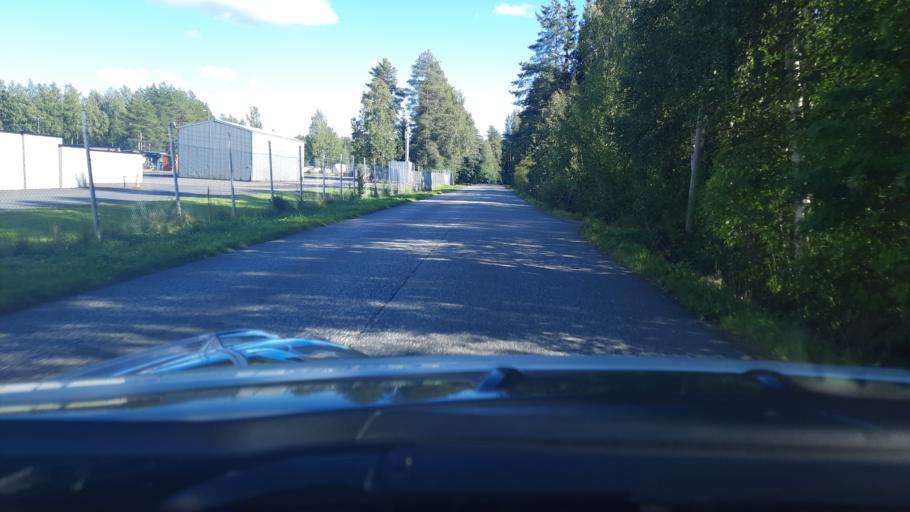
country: FI
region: North Karelia
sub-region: Joensuu
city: Joensuu
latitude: 62.6364
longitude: 29.6948
